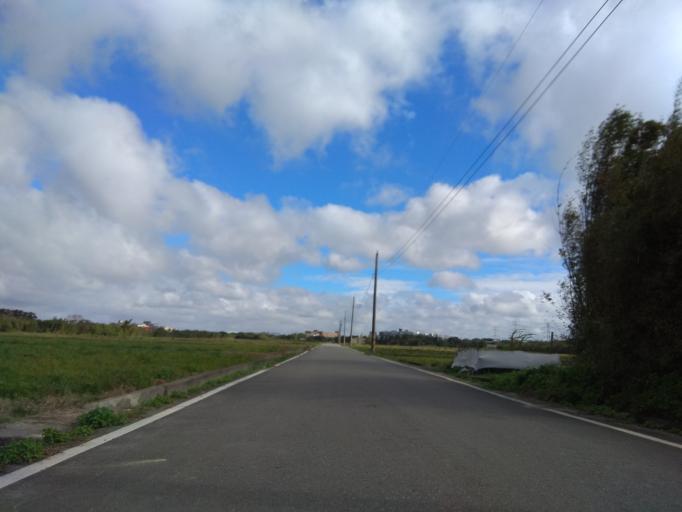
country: TW
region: Taiwan
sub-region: Hsinchu
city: Zhubei
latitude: 24.9715
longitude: 121.0797
